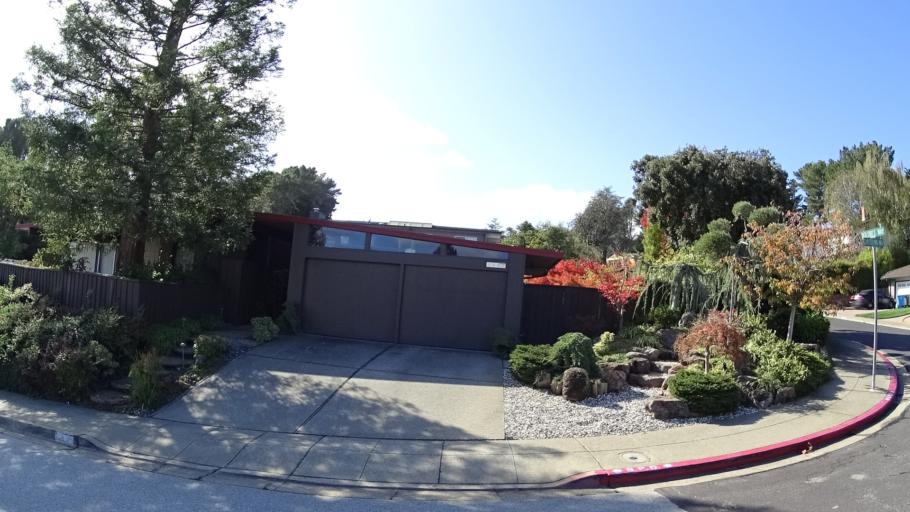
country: US
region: California
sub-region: San Mateo County
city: Millbrae
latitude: 37.5838
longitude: -122.3978
